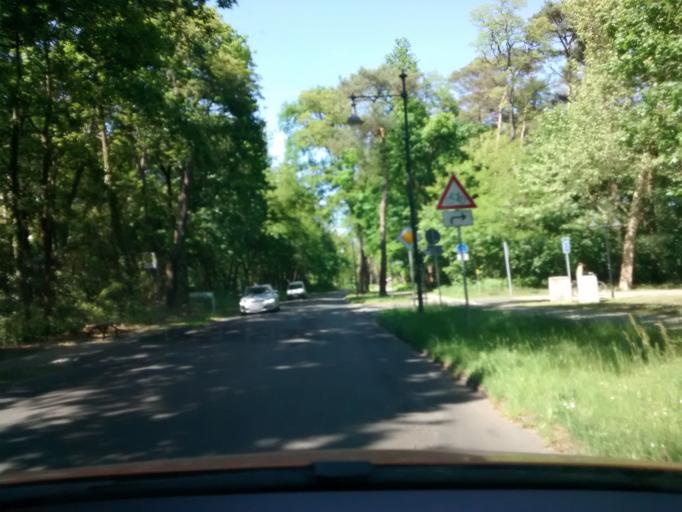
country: DE
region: Brandenburg
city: Bad Saarow
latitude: 52.2811
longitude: 14.0387
